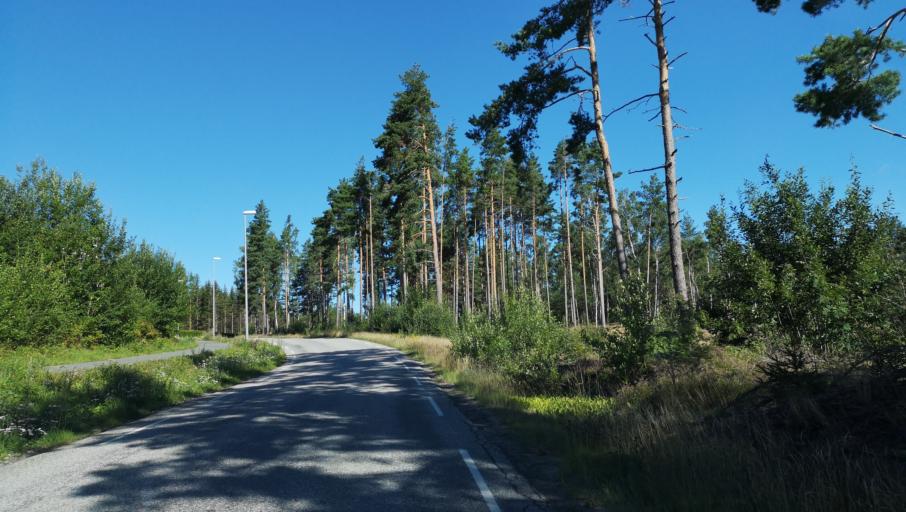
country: NO
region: Ostfold
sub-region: Hobol
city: Knappstad
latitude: 59.6308
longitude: 11.0261
